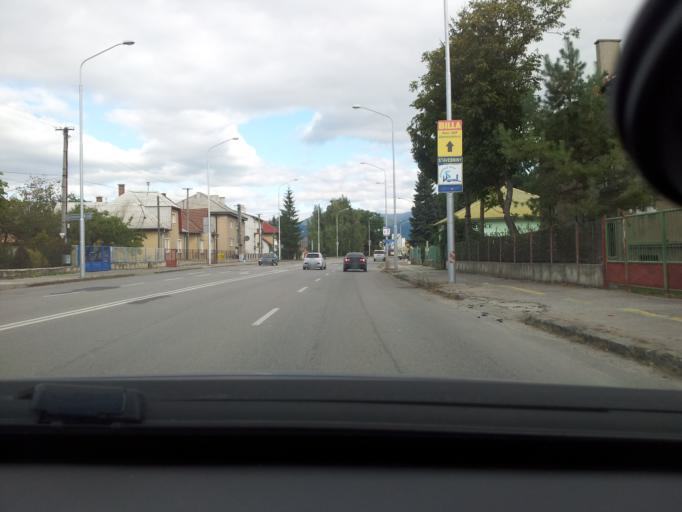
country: SK
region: Zilinsky
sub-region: Okres Martin
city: Martin
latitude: 49.0534
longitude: 18.9150
